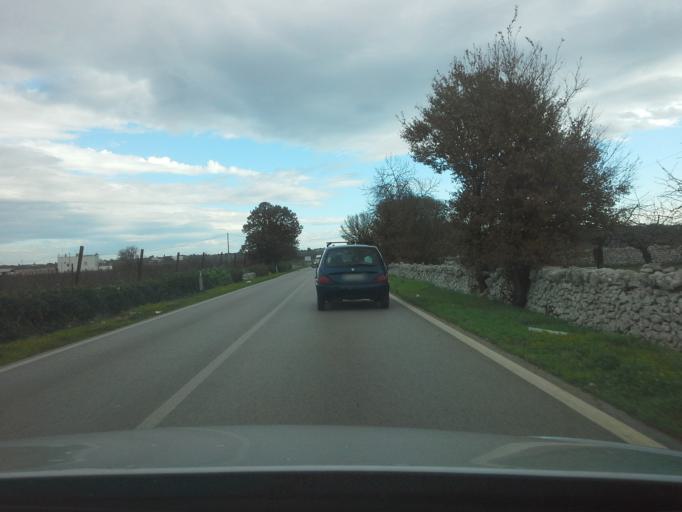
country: IT
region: Apulia
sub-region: Provincia di Bari
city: Putignano
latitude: 40.8776
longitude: 17.0708
